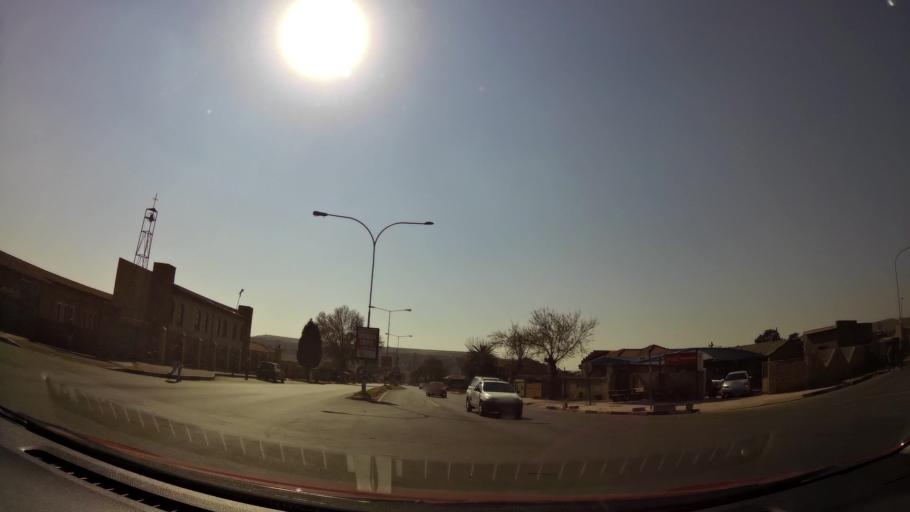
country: ZA
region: Gauteng
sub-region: City of Johannesburg Metropolitan Municipality
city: Soweto
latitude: -26.2400
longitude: 27.9503
